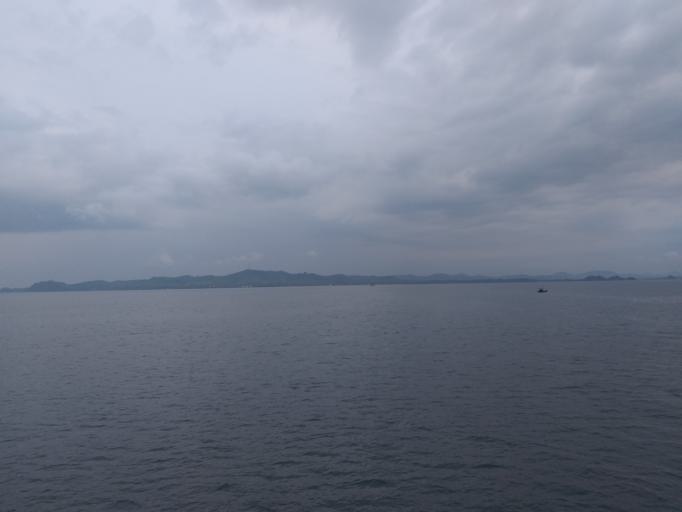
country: TH
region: Trat
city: Laem Ngop
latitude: 12.1515
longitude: 102.2859
